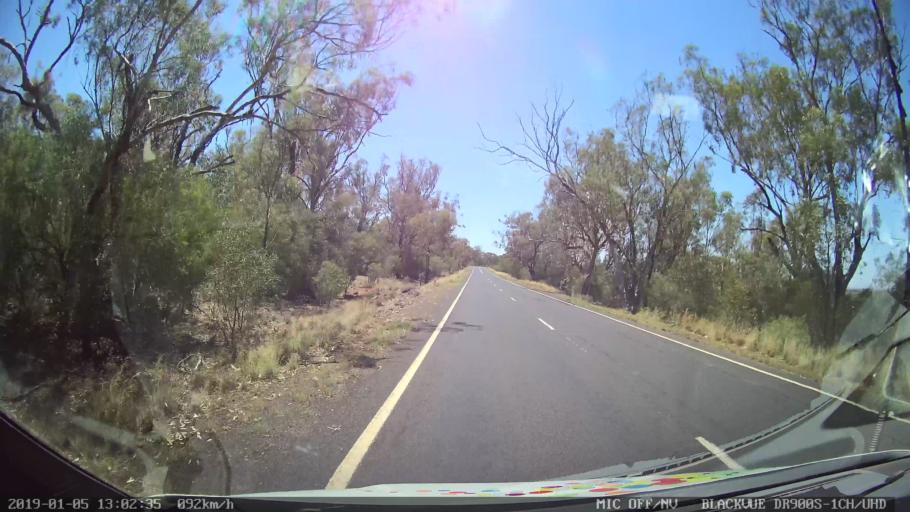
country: AU
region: New South Wales
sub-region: Gunnedah
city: Gunnedah
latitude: -31.1142
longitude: 149.8139
